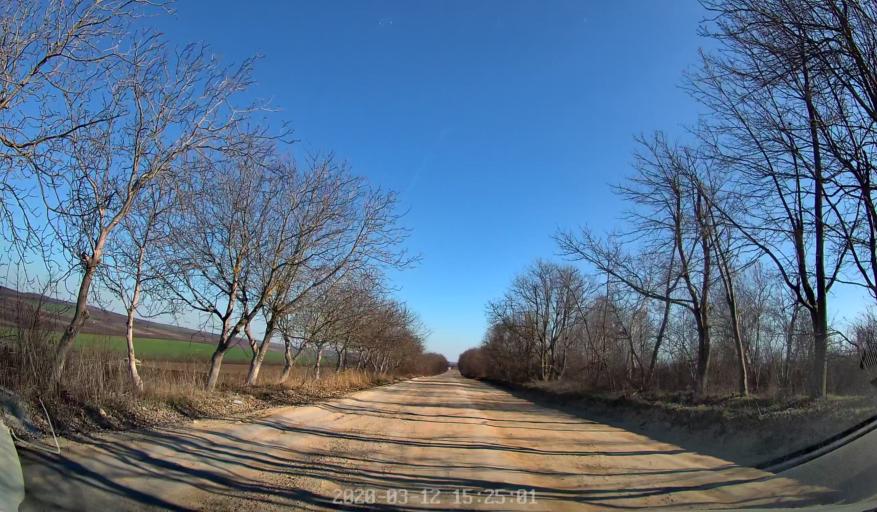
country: MD
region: Chisinau
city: Ciorescu
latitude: 47.1843
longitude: 28.9162
